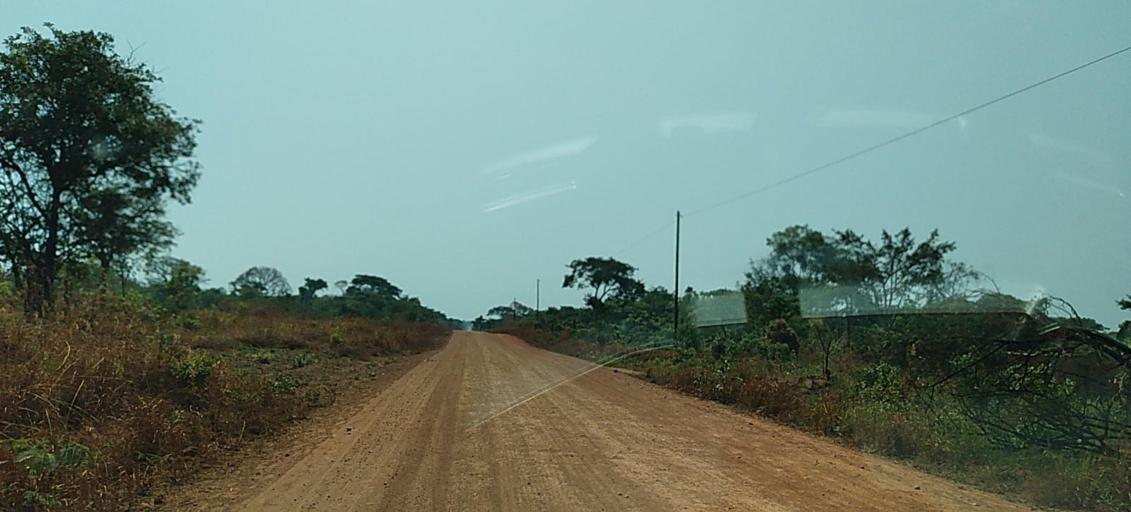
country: ZM
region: North-Western
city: Kansanshi
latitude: -11.9926
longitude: 26.6213
